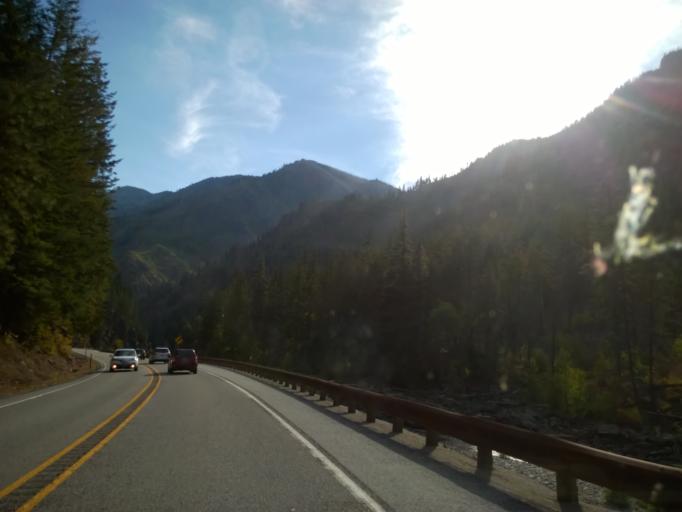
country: US
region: Washington
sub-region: Chelan County
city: Leavenworth
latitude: 47.6363
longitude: -120.7253
